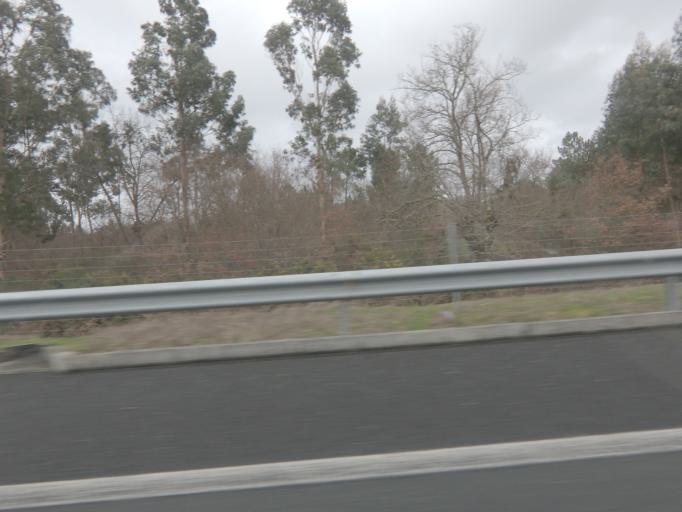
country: ES
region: Galicia
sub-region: Provincia de Pontevedra
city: Silleda
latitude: 42.6920
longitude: -8.1903
